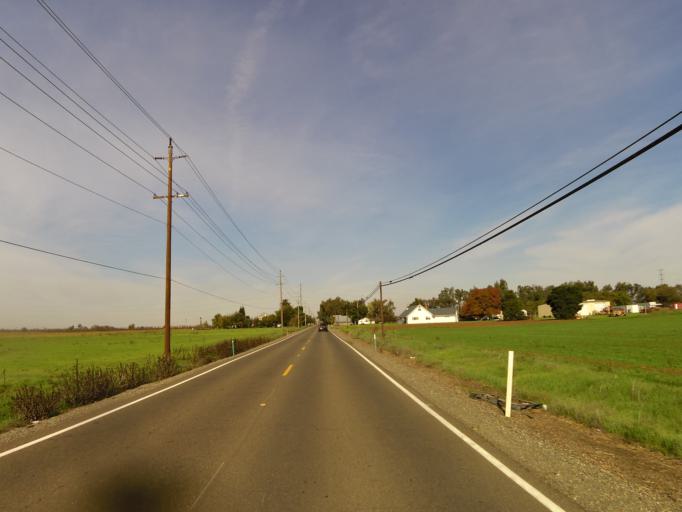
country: US
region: California
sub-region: Sacramento County
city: Laguna
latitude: 38.3532
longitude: -121.4175
